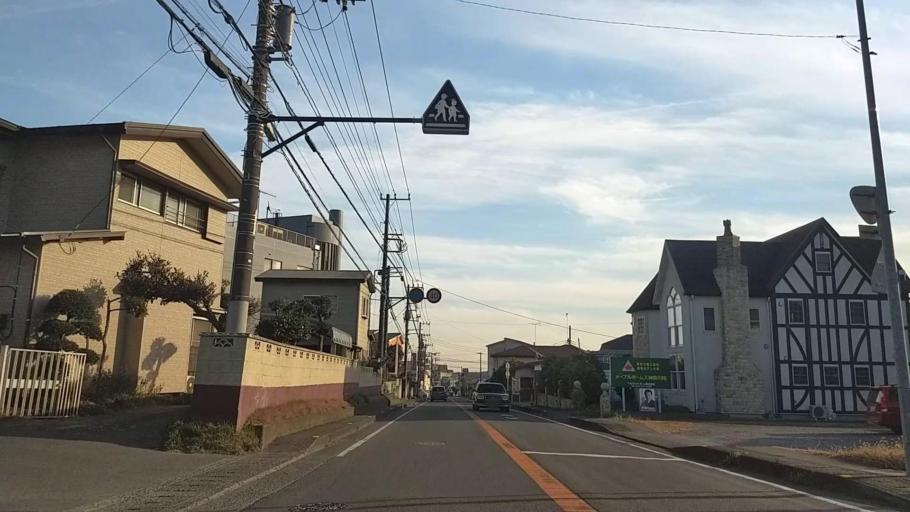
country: JP
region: Kanagawa
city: Zama
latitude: 35.4989
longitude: 139.3138
